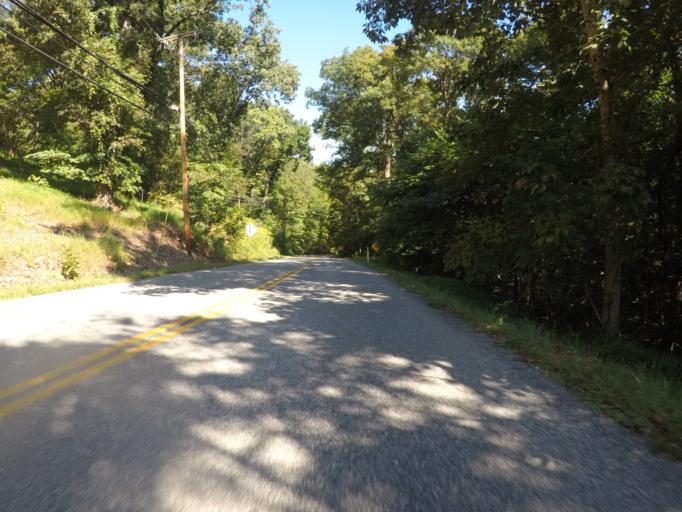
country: US
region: Kentucky
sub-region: Greenup County
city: Russell
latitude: 38.5204
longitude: -82.6951
